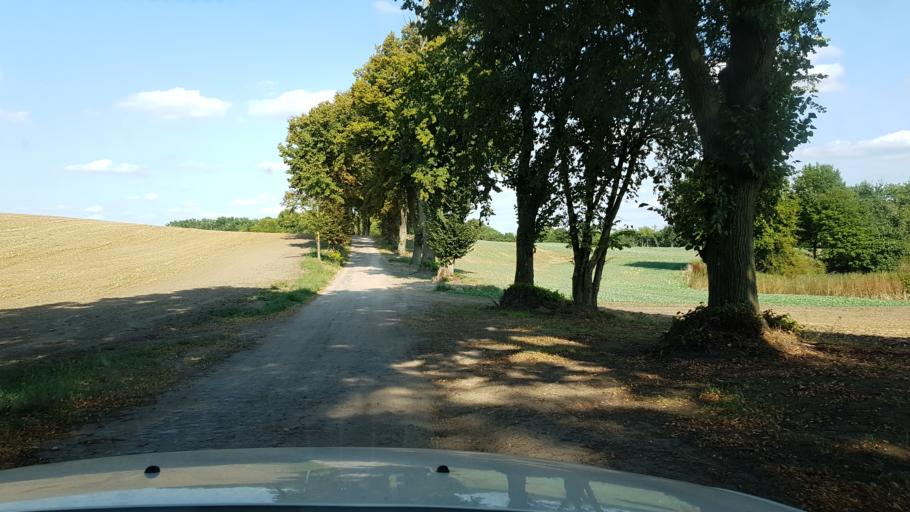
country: PL
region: West Pomeranian Voivodeship
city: Trzcinsko Zdroj
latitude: 52.9072
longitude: 14.5831
